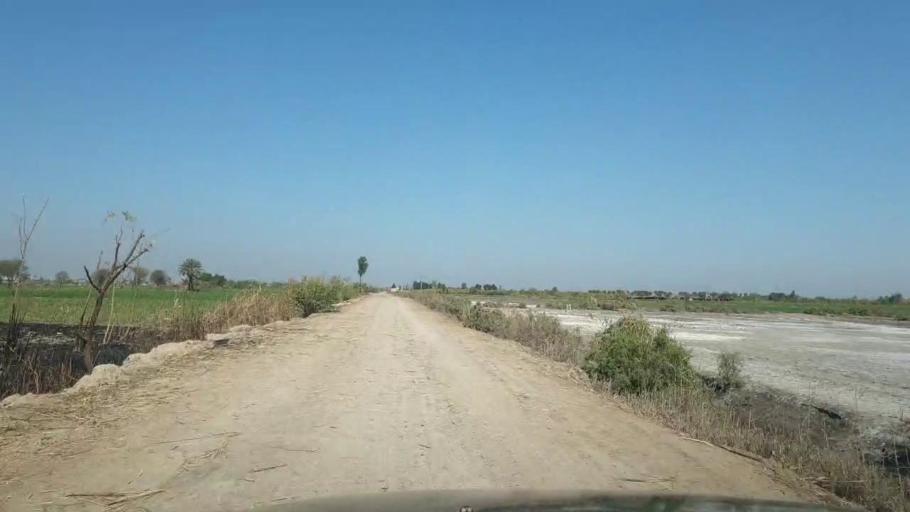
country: PK
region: Sindh
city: Mirpur Khas
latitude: 25.5941
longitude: 69.0555
